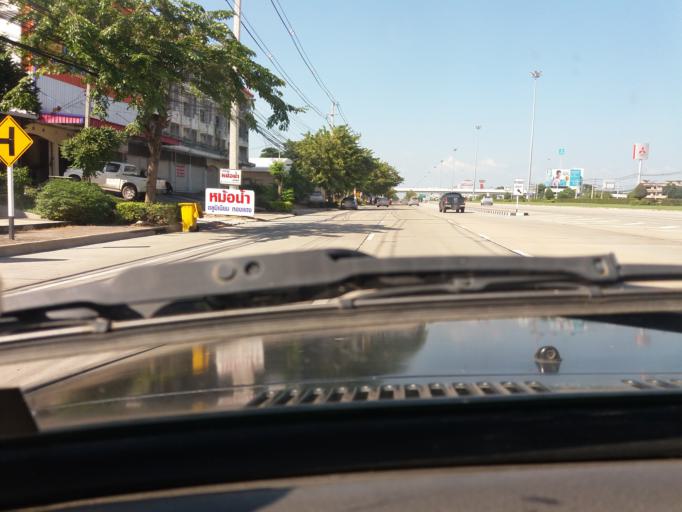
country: TH
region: Suphan Buri
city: Suphan Buri
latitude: 14.4618
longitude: 100.1311
